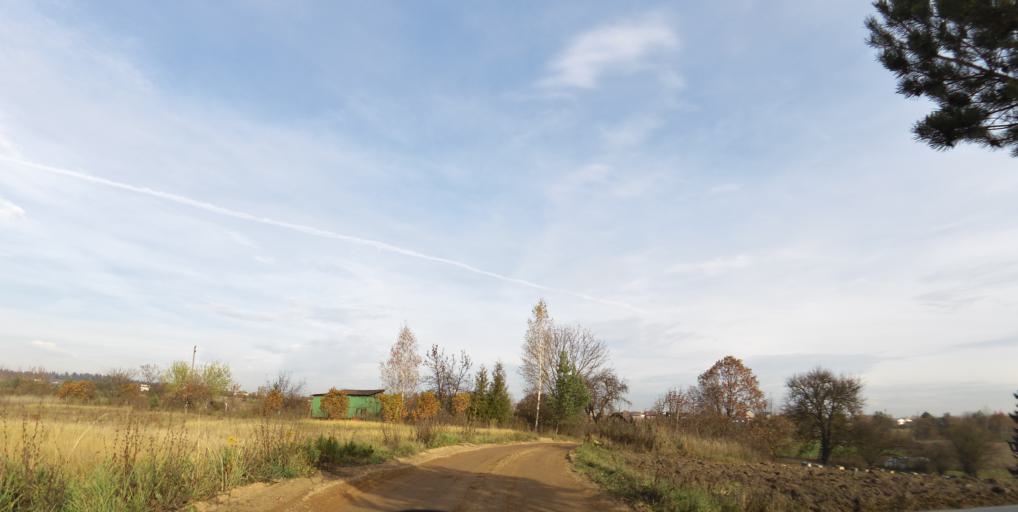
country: LT
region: Vilnius County
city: Pilaite
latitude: 54.7239
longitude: 25.1634
